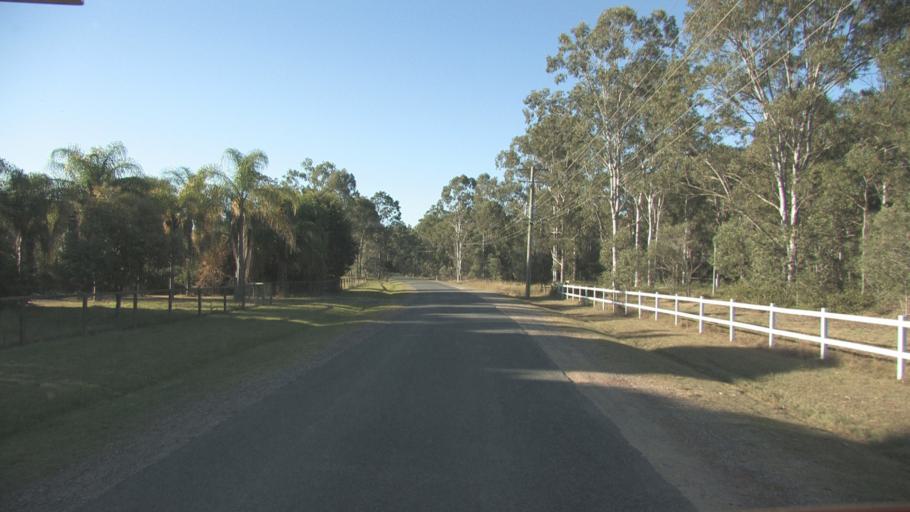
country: AU
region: Queensland
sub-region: Logan
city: Chambers Flat
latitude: -27.7775
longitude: 153.1282
